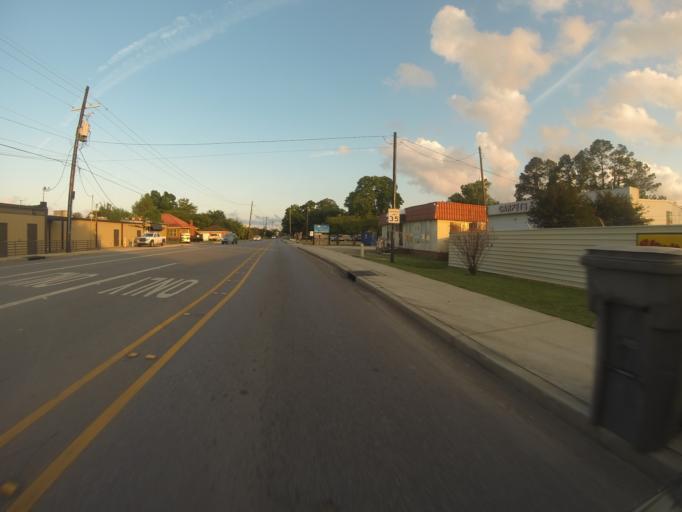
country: US
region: Louisiana
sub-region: Lafayette Parish
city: Lafayette
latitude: 30.2030
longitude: -92.0484
